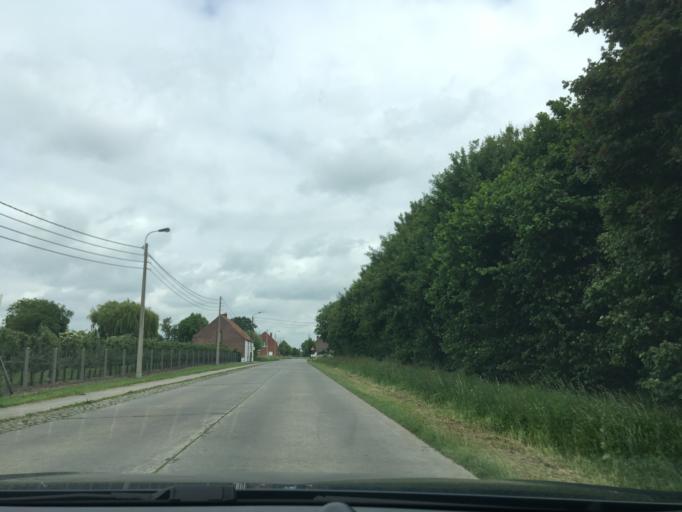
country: BE
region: Flanders
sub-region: Provincie West-Vlaanderen
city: Menen
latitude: 50.8242
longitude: 3.0859
